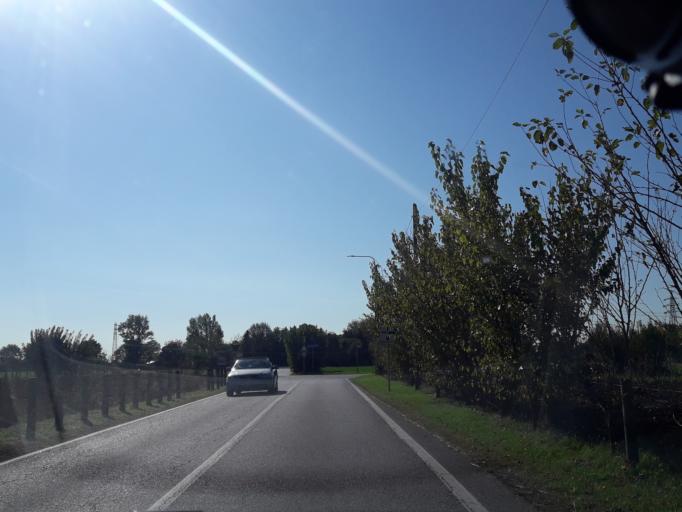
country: IT
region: Friuli Venezia Giulia
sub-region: Provincia di Udine
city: Udine
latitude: 46.0695
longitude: 13.2825
